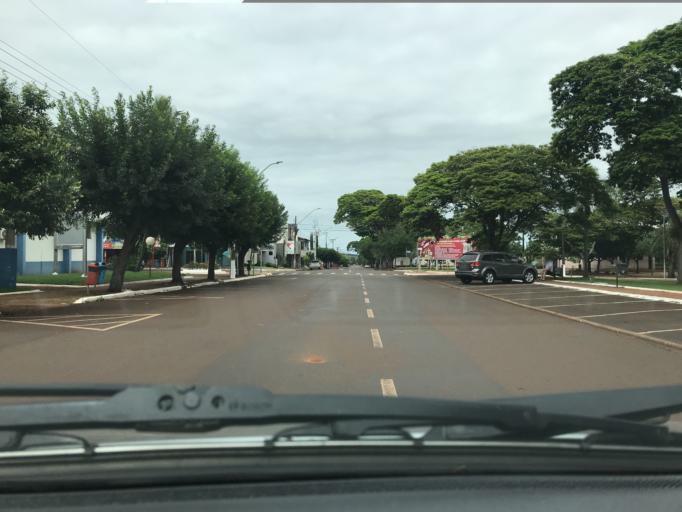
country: BR
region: Parana
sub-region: Palotina
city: Palotina
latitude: -24.2844
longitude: -53.8402
